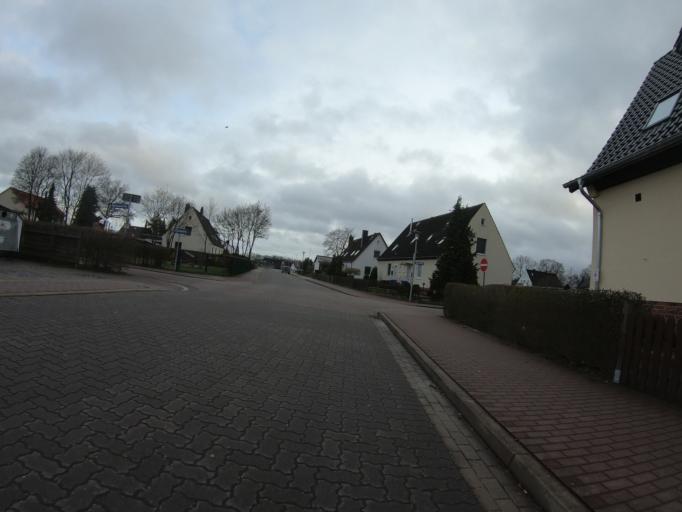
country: DE
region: Lower Saxony
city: Wesendorf
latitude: 52.5943
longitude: 10.5380
